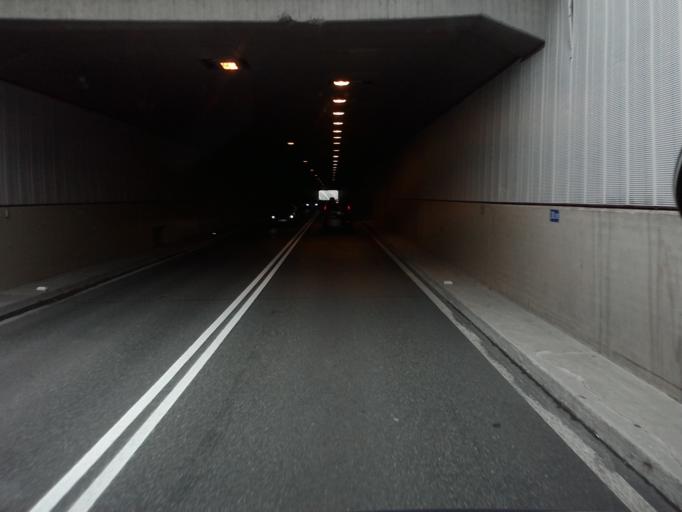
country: AT
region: Tyrol
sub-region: Politischer Bezirk Kitzbuhel
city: Sankt Johann in Tirol
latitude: 47.5219
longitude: 12.4203
